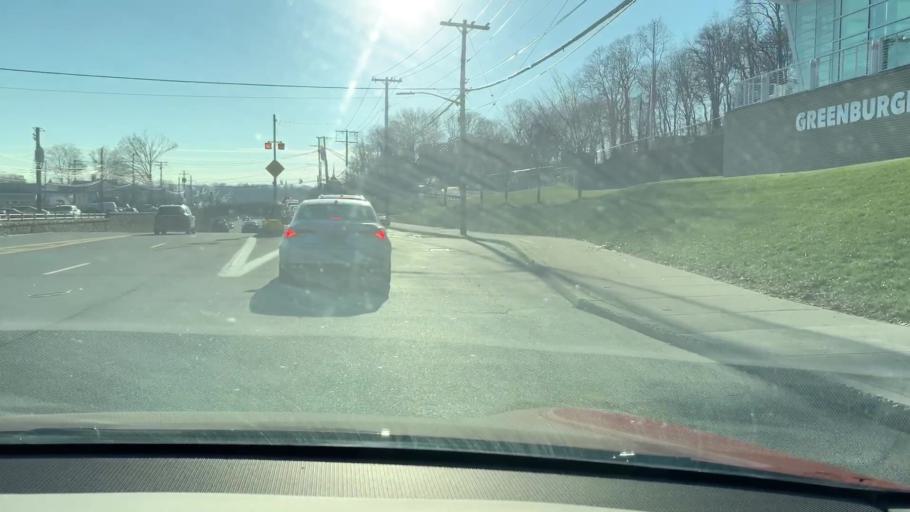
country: US
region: New York
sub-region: Westchester County
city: Fairview
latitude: 41.0468
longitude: -73.8066
